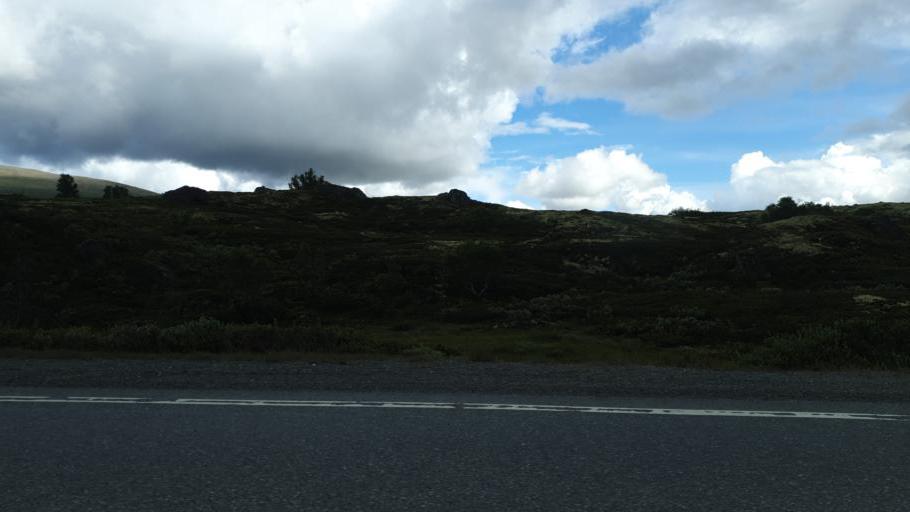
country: NO
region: Sor-Trondelag
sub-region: Oppdal
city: Oppdal
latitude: 62.2809
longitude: 9.5997
